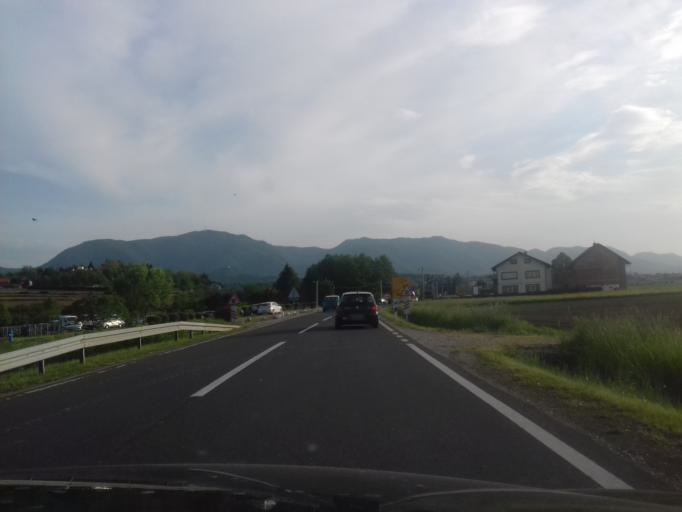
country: HR
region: Varazdinska
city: Ivanec
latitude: 46.2376
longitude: 16.1573
